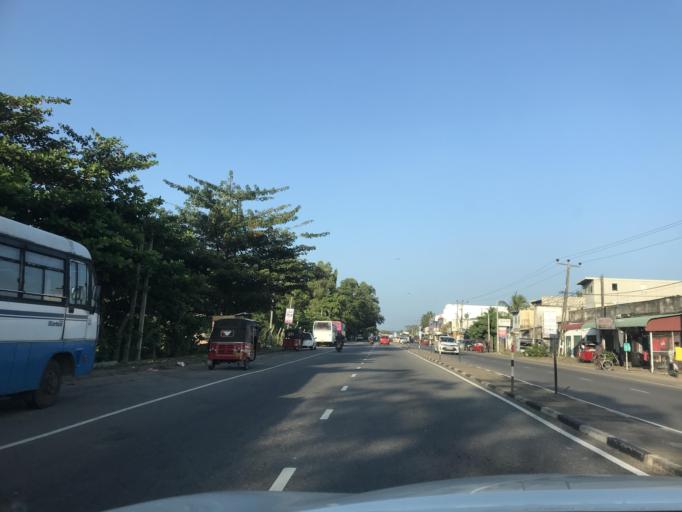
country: LK
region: Western
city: Ja Ela
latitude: 7.0958
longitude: 79.9057
